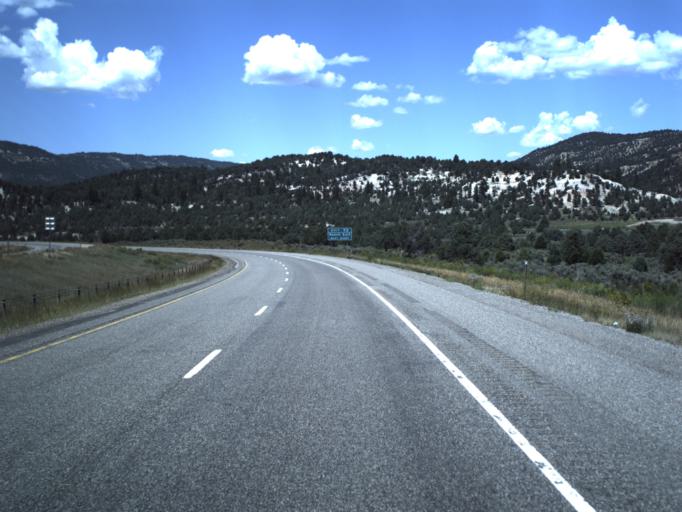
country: US
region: Utah
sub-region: Sevier County
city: Salina
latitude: 38.8733
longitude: -111.5536
